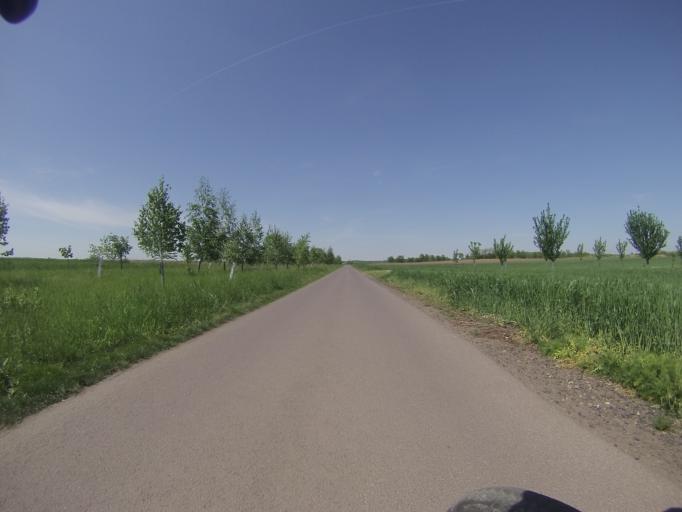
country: CZ
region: South Moravian
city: Novosedly
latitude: 48.8073
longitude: 16.4864
